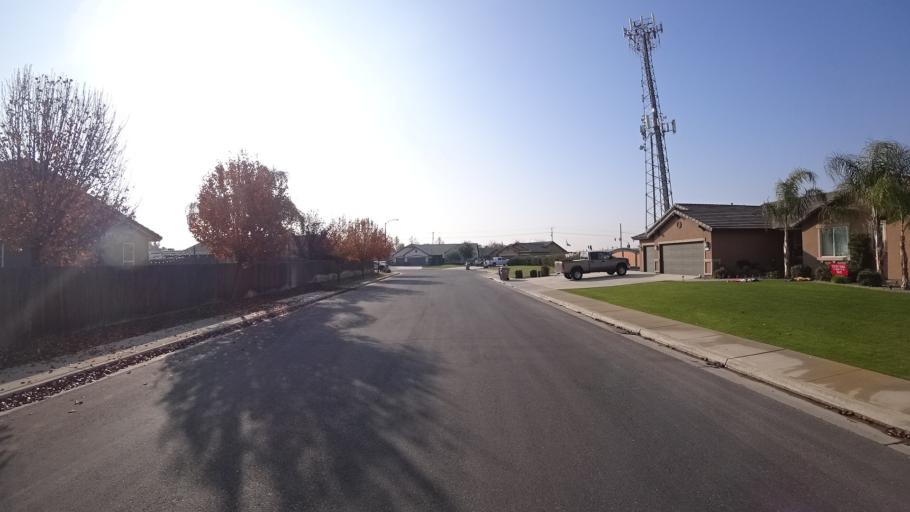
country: US
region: California
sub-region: Kern County
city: Greenacres
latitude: 35.4284
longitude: -119.1205
